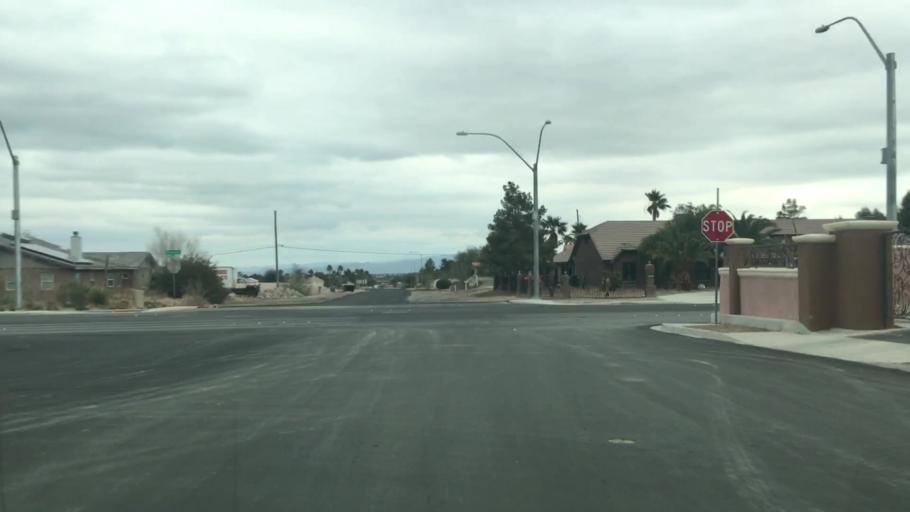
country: US
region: Nevada
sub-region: Clark County
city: Paradise
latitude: 36.0496
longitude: -115.1549
